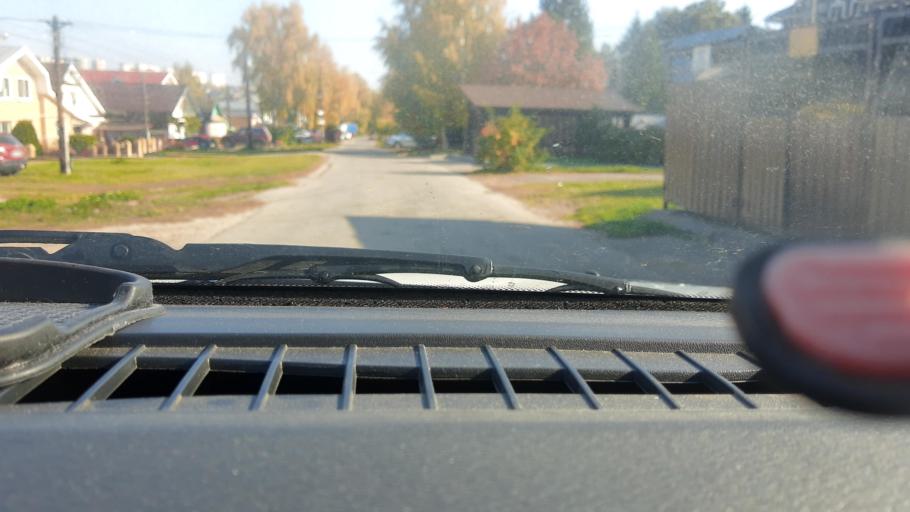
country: RU
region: Nizjnij Novgorod
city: Afonino
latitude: 56.2758
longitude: 44.0390
